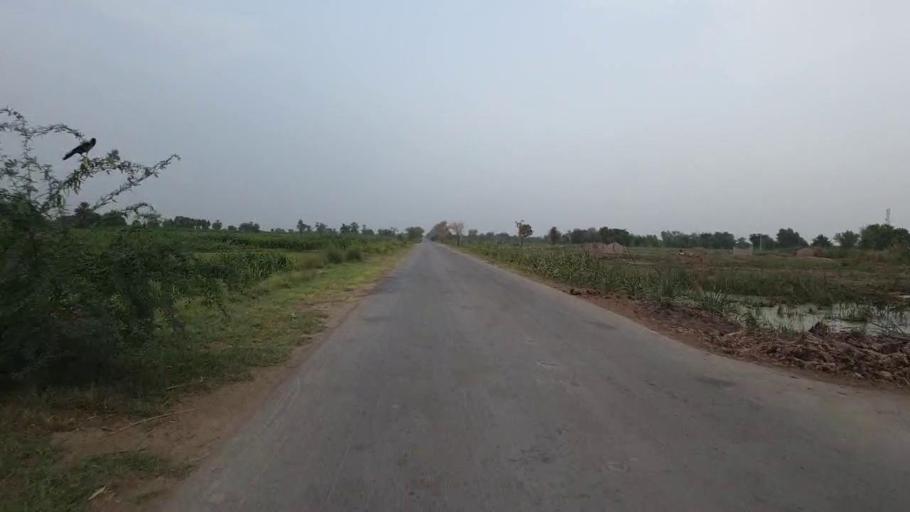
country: PK
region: Sindh
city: Daur
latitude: 26.4050
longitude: 68.2263
